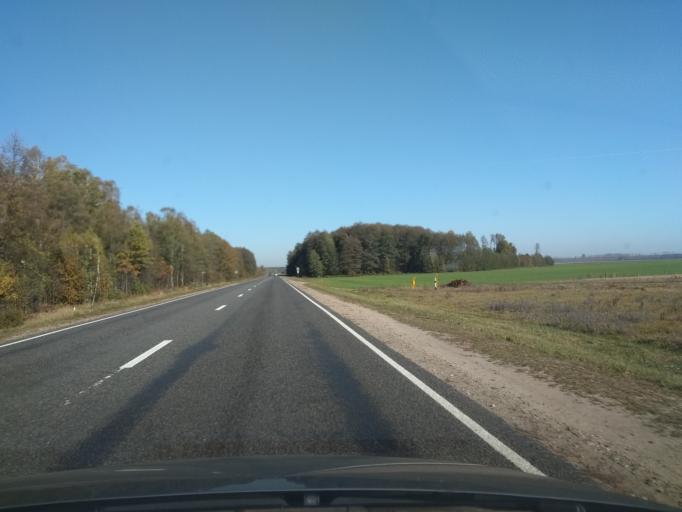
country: BY
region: Brest
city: Malaryta
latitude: 51.9913
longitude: 24.2087
